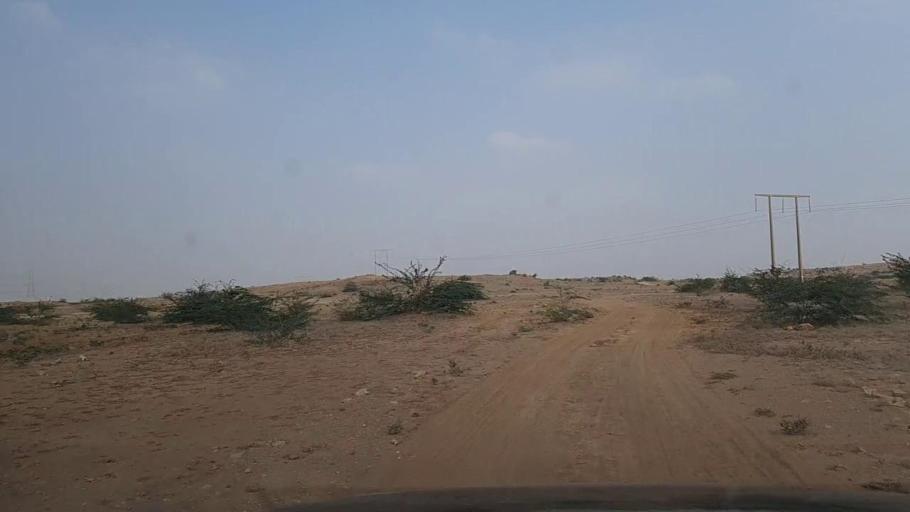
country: PK
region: Sindh
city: Thatta
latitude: 24.8878
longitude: 67.8399
